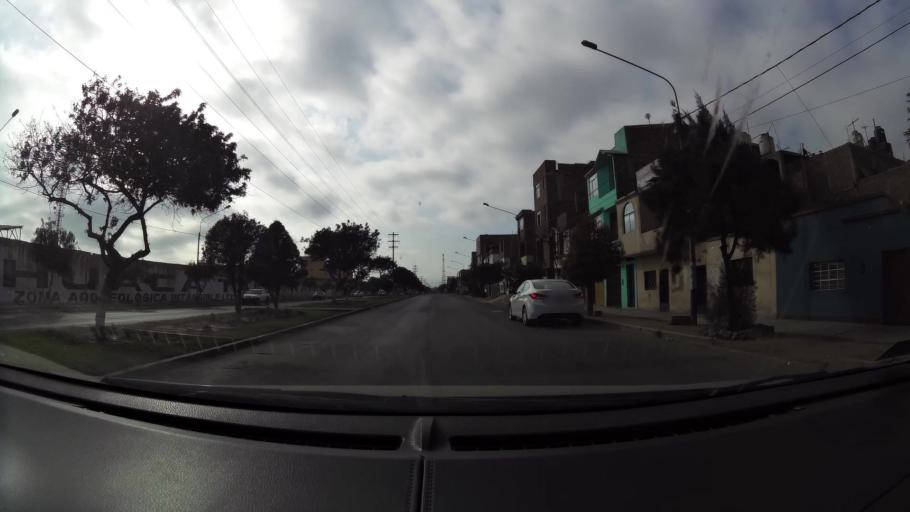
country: PE
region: La Libertad
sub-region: Provincia de Trujillo
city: La Esperanza
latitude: -8.0798
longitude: -79.0447
